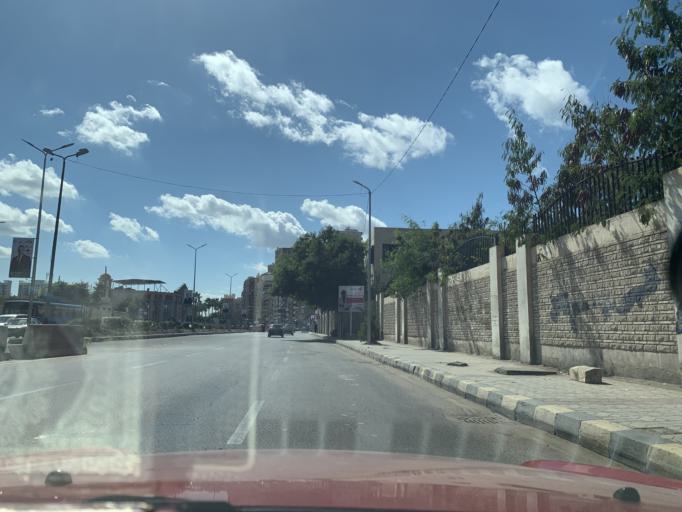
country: EG
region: Alexandria
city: Alexandria
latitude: 31.2202
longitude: 29.9479
